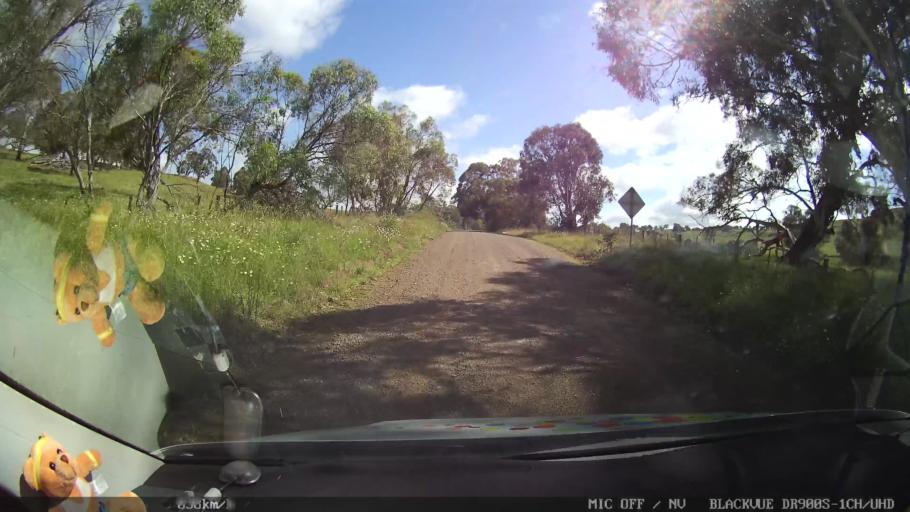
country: AU
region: New South Wales
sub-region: Guyra
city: Guyra
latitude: -29.9817
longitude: 151.6962
